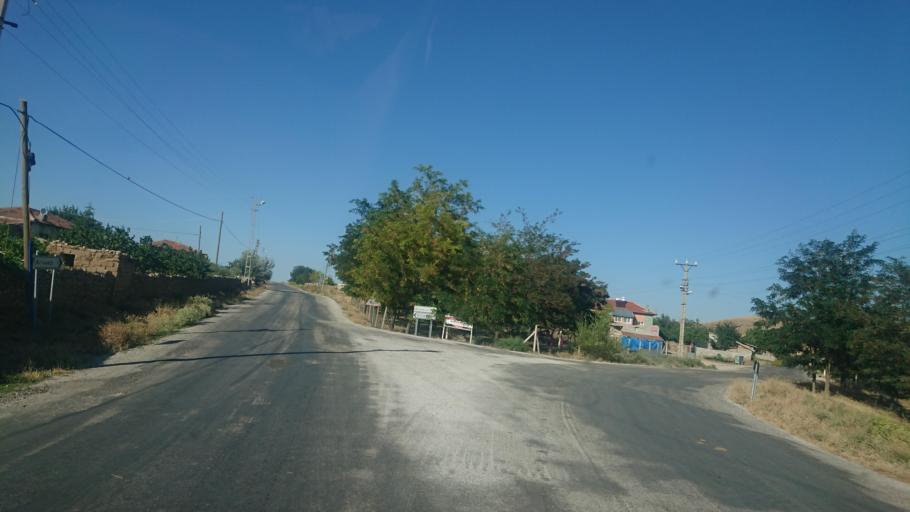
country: TR
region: Aksaray
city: Agacoren
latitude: 38.7704
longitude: 33.7044
